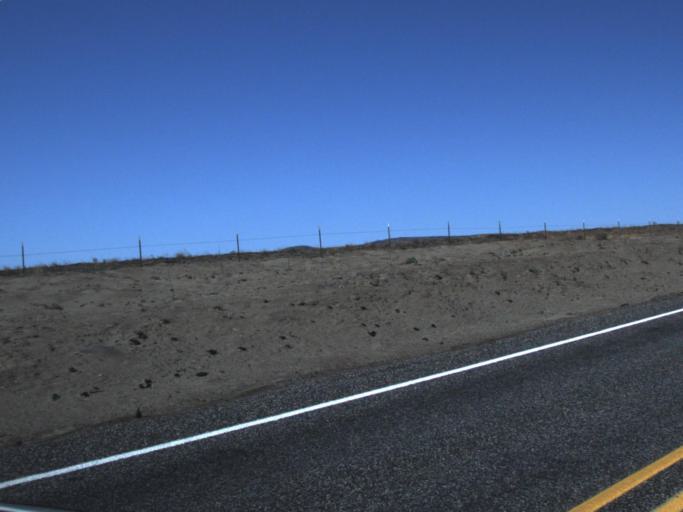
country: US
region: Washington
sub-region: Grant County
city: Desert Aire
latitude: 46.5703
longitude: -119.7266
